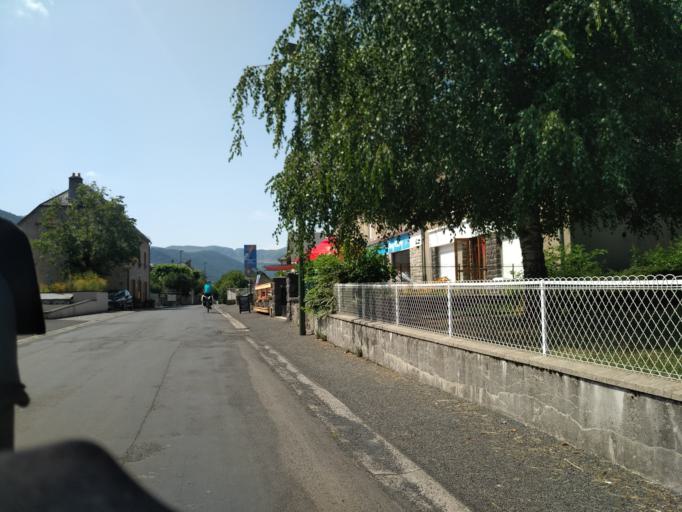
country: FR
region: Auvergne
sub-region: Departement du Cantal
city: Riom-es-Montagnes
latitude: 45.1595
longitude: 2.7059
